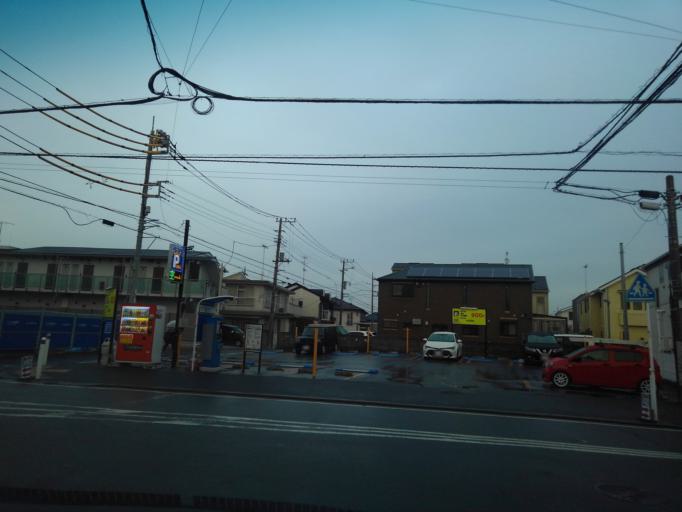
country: JP
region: Tokyo
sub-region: Machida-shi
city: Machida
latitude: 35.5201
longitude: 139.4429
